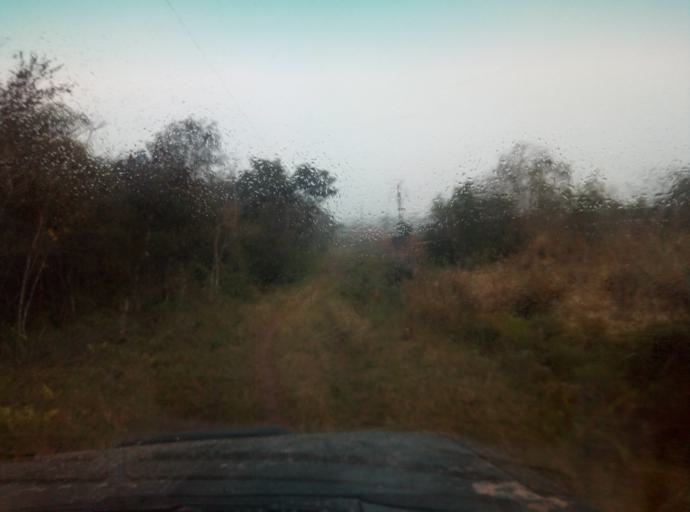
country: PY
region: Caaguazu
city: Doctor Cecilio Baez
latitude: -25.1520
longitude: -56.2607
